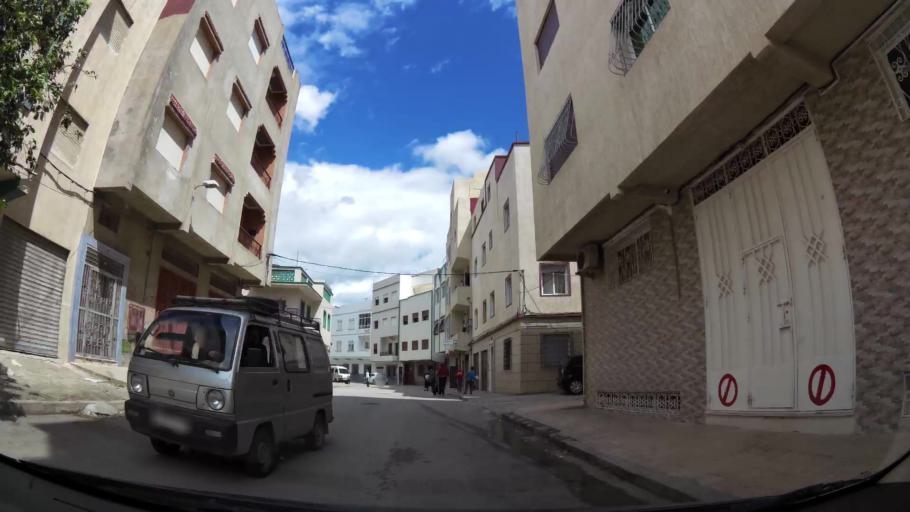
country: MA
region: Tanger-Tetouan
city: Tetouan
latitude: 35.5738
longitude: -5.3527
